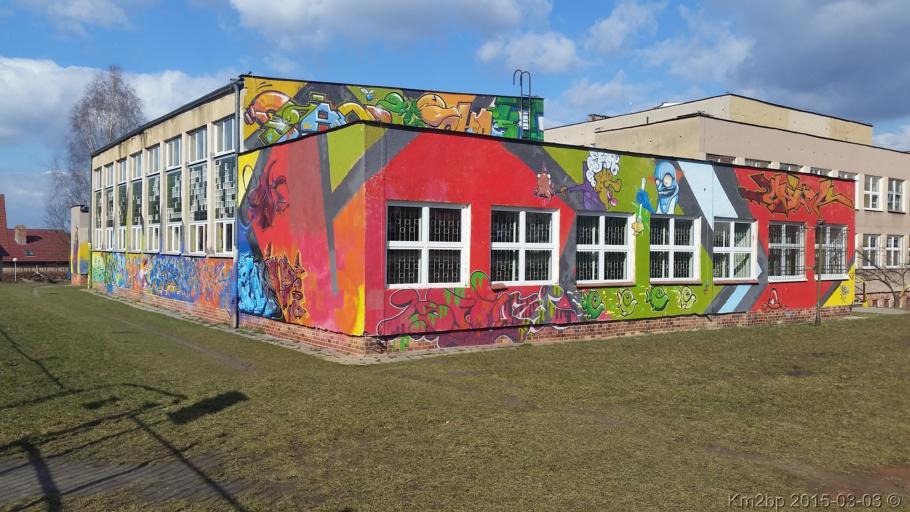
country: PL
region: Lubusz
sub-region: Zielona Gora
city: Zielona Gora
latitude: 51.9340
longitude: 15.4734
